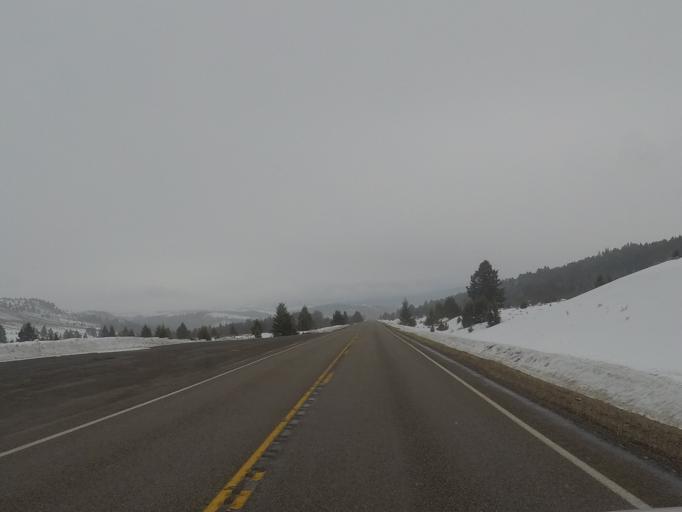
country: US
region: Montana
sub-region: Meagher County
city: White Sulphur Springs
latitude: 46.6437
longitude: -110.8645
